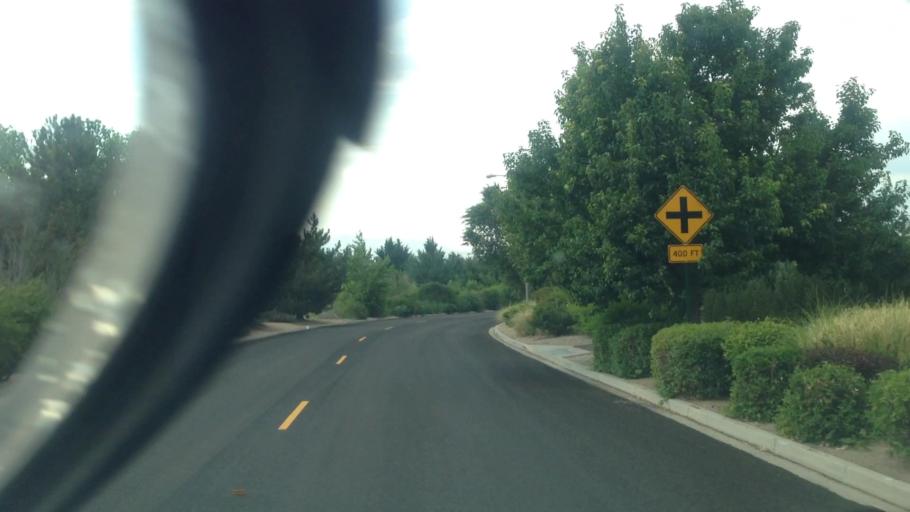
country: US
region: Nevada
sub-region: Washoe County
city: Lemmon Valley
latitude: 39.6317
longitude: -119.8758
